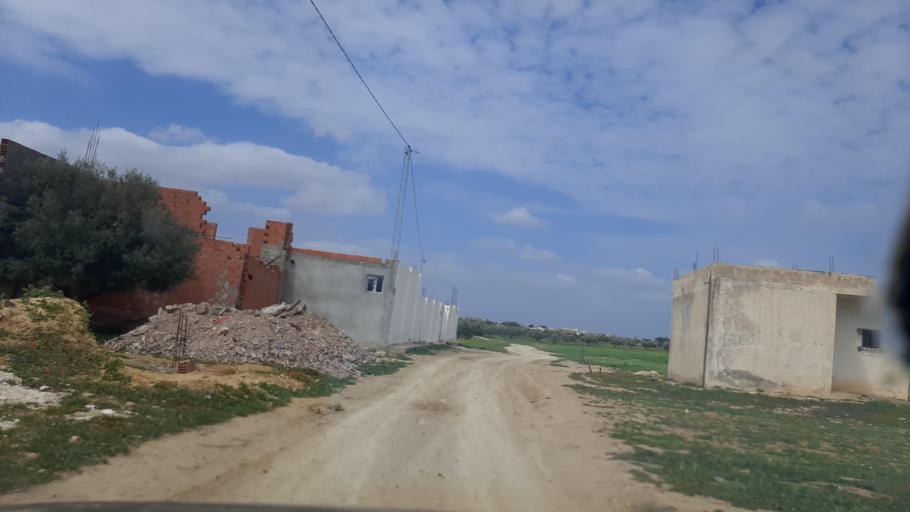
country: TN
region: Tunis
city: Oued Lill
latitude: 36.6875
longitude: 9.9972
